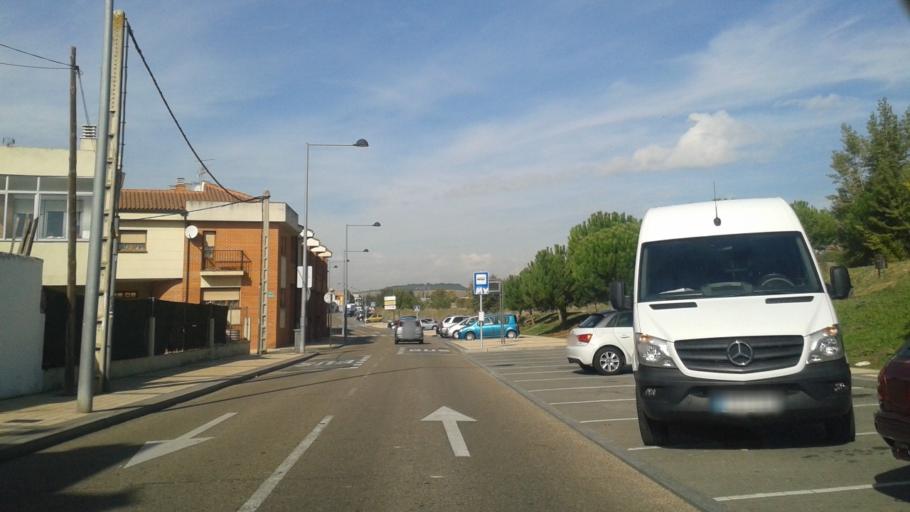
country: ES
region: Castille and Leon
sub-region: Provincia de Valladolid
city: Arroyo
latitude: 41.6277
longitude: -4.7696
